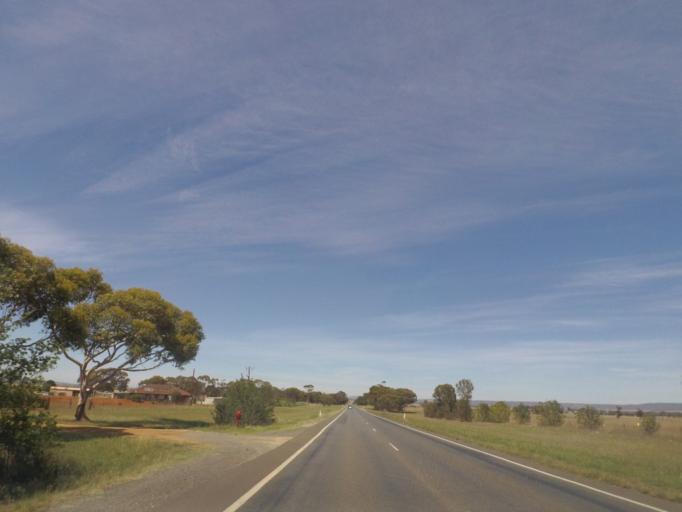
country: AU
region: Victoria
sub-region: Moorabool
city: Bacchus Marsh
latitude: -37.7901
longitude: 144.4199
